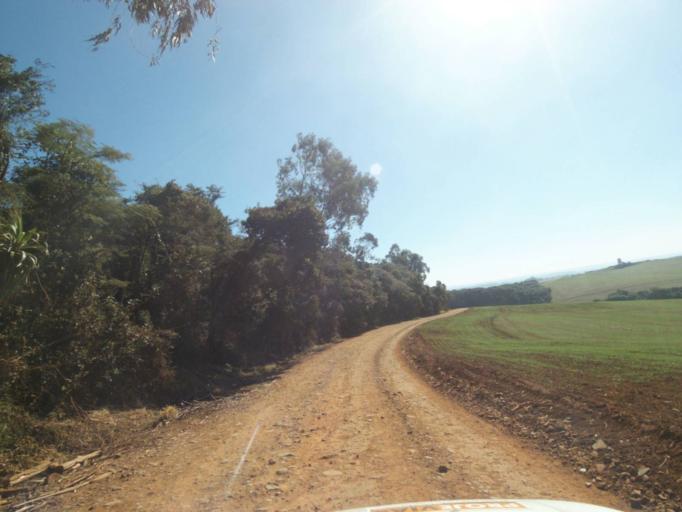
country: BR
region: Parana
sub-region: Tibagi
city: Tibagi
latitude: -24.5730
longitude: -50.6241
